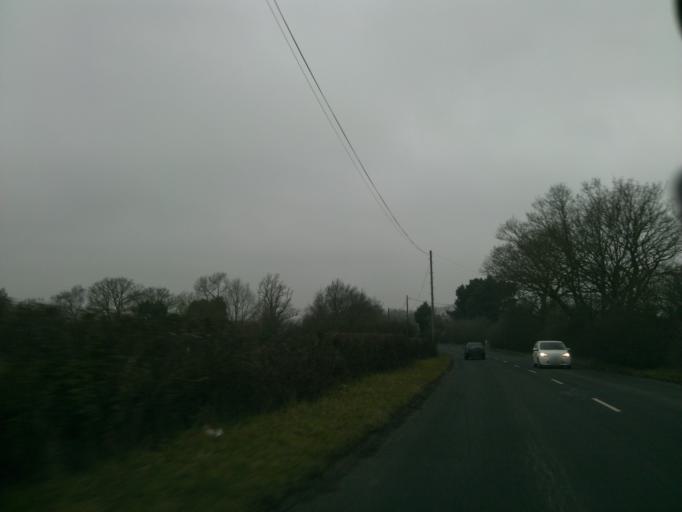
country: GB
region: England
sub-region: Essex
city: Alresford
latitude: 51.8813
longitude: 1.0204
